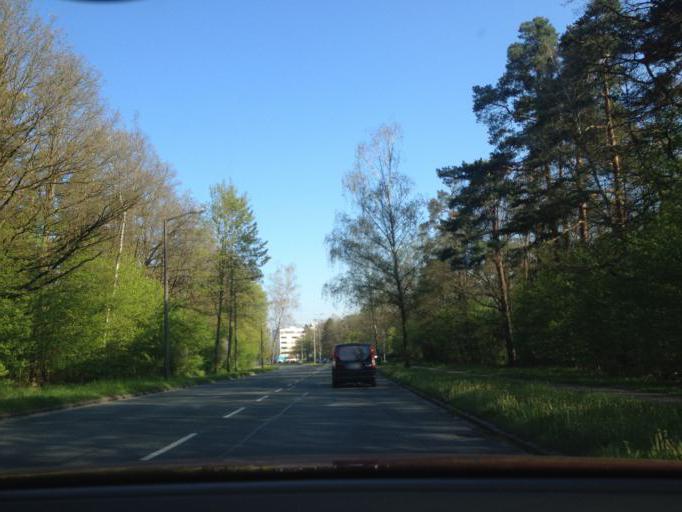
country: DE
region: Bavaria
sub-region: Regierungsbezirk Mittelfranken
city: Wendelstein
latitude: 49.3954
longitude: 11.1259
